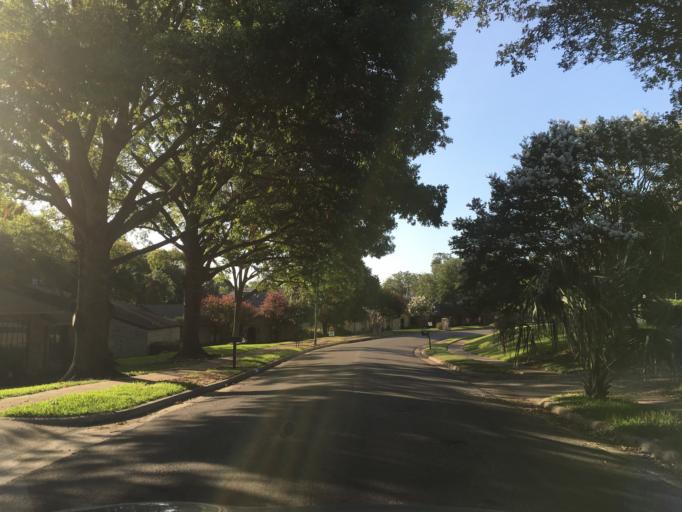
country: US
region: Texas
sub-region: Dallas County
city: Richardson
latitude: 32.8869
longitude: -96.7353
